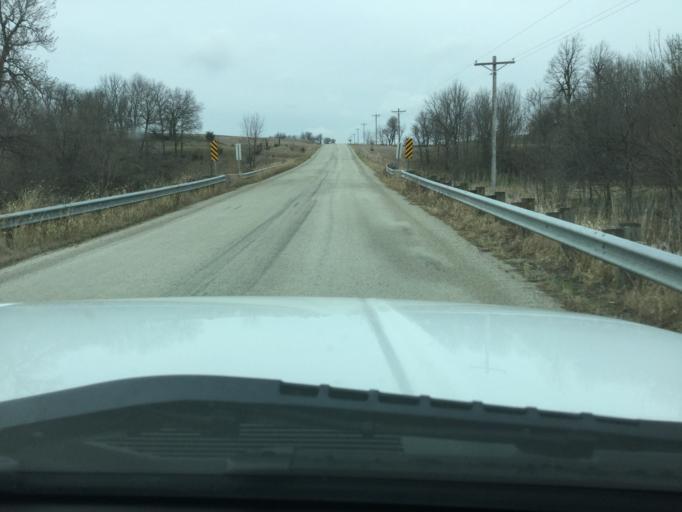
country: US
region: Kansas
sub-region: Nemaha County
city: Sabetha
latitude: 39.8911
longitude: -95.7139
